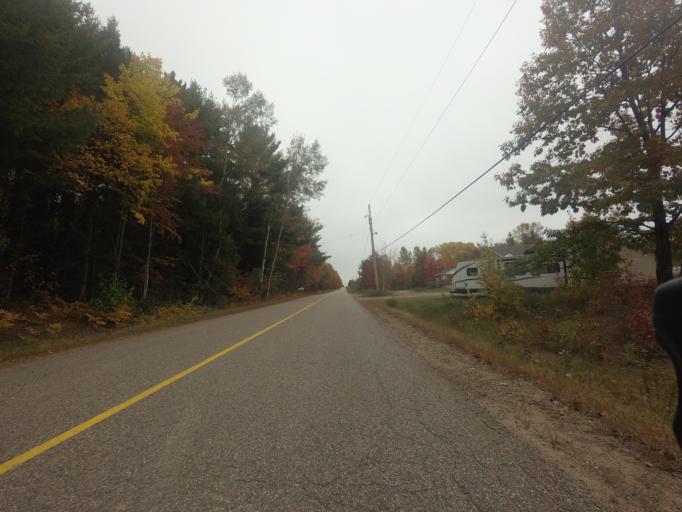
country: CA
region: Ontario
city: Petawawa
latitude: 45.7553
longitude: -77.2560
